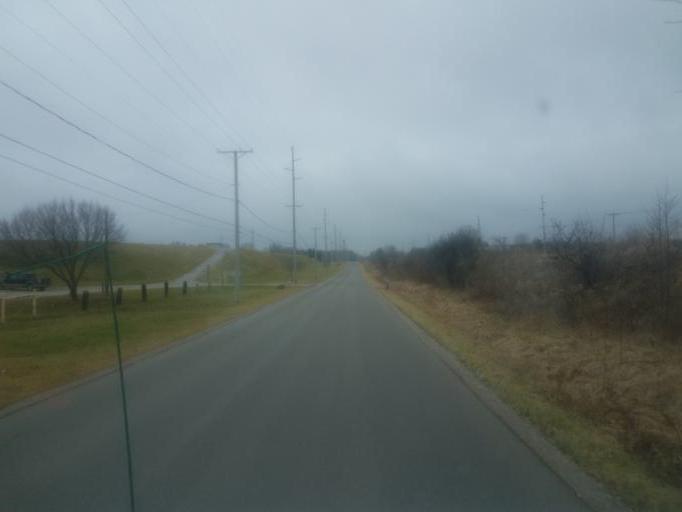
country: US
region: Ohio
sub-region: Crawford County
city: Galion
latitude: 40.7230
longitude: -82.8019
